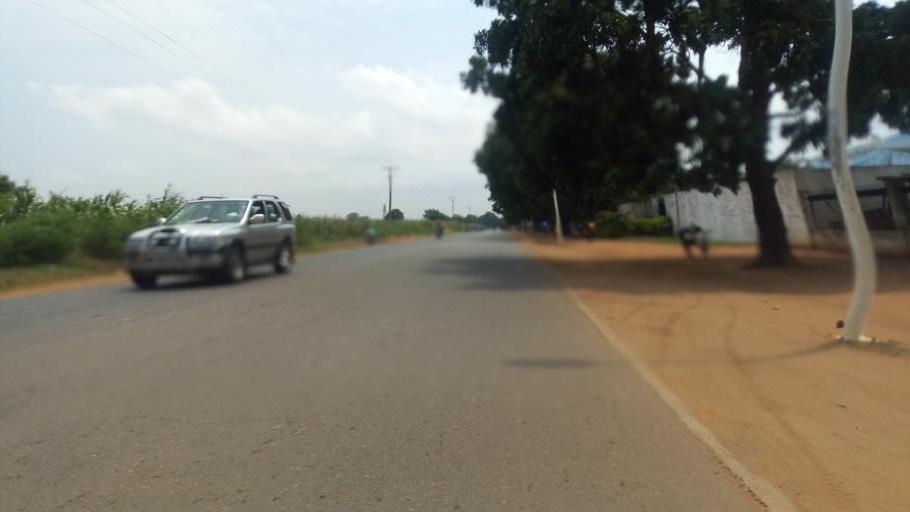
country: TG
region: Maritime
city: Lome
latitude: 6.1911
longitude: 1.2357
